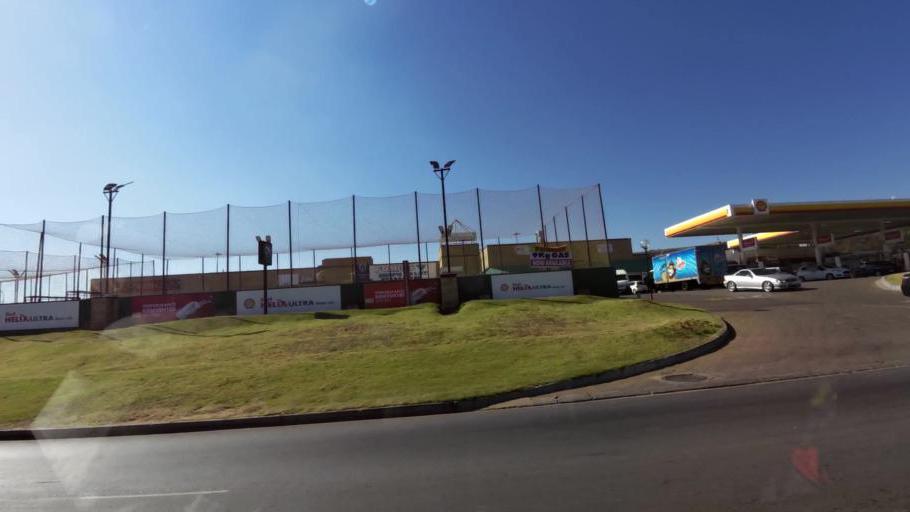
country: ZA
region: Gauteng
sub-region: City of Johannesburg Metropolitan Municipality
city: Johannesburg
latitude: -26.2503
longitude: 27.9714
